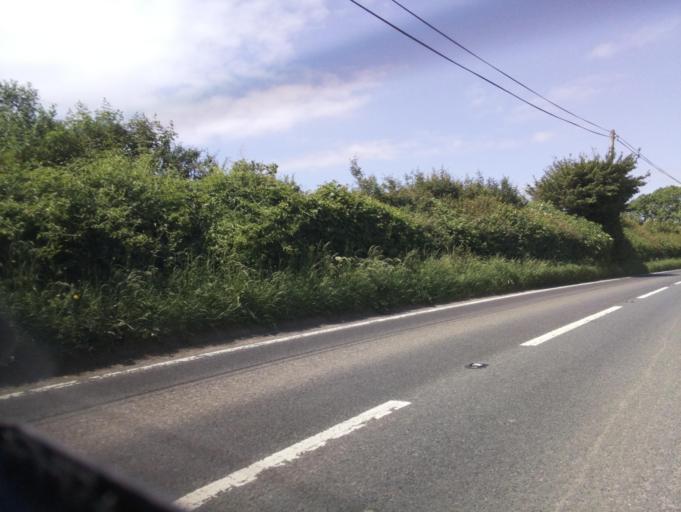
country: GB
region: England
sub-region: Somerset
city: Wincanton
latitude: 51.0579
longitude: -2.4542
